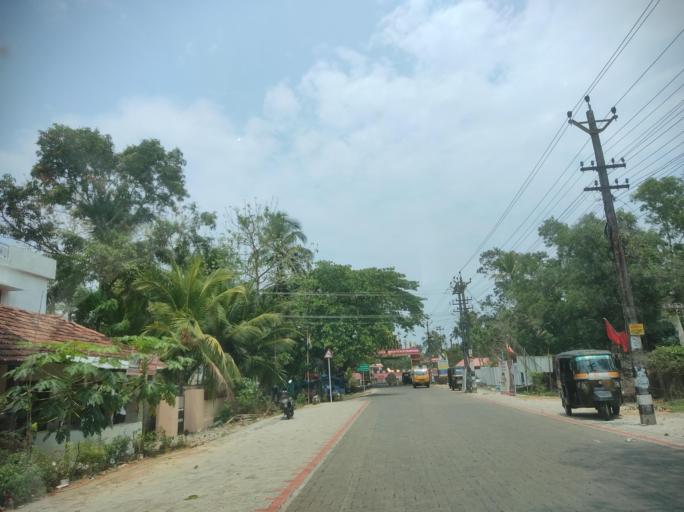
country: IN
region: Kerala
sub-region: Alappuzha
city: Vayalar
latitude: 9.7080
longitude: 76.3259
